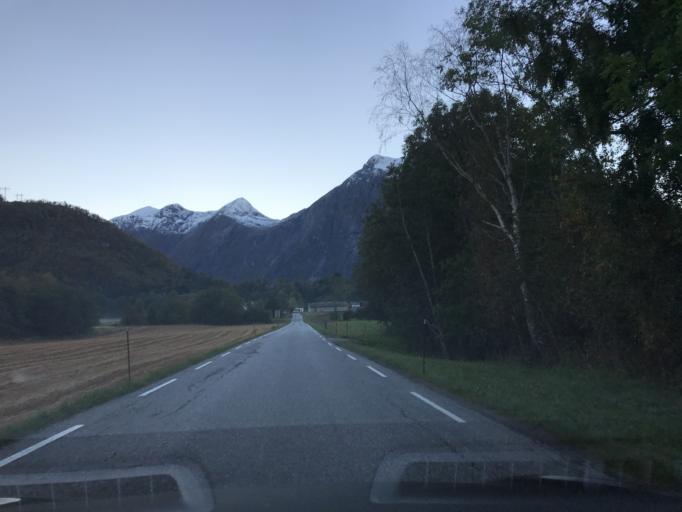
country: NO
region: More og Romsdal
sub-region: Rauma
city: Andalsnes
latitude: 62.5298
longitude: 7.7335
